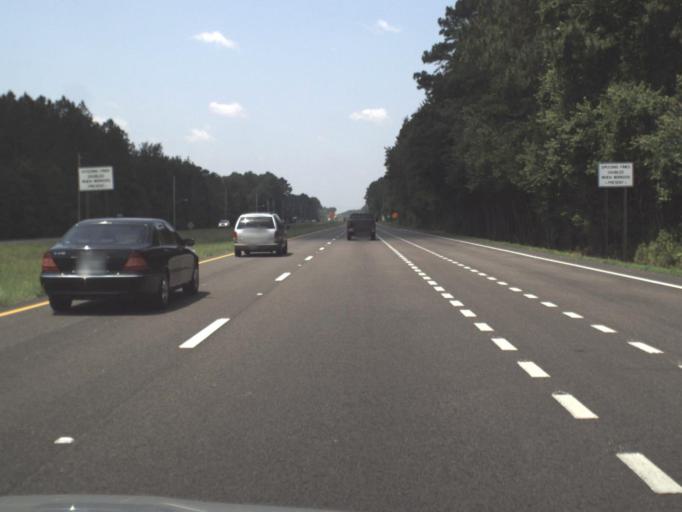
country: US
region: Florida
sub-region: Duval County
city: Baldwin
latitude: 30.2672
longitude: -81.8493
